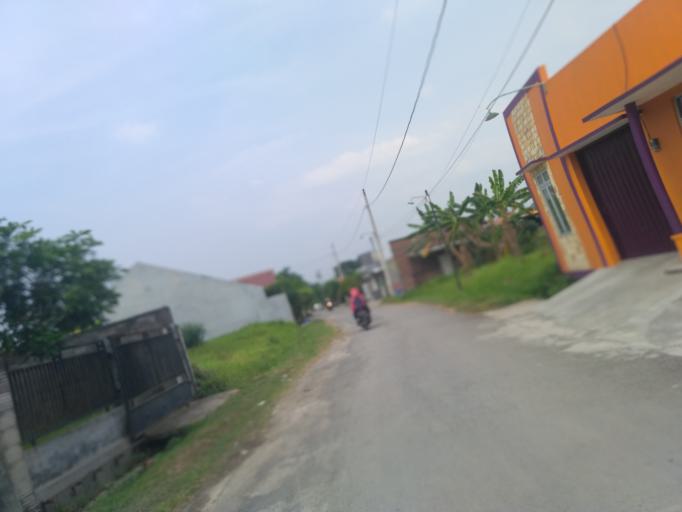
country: ID
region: Central Java
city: Mranggen
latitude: -7.0633
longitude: 110.4665
